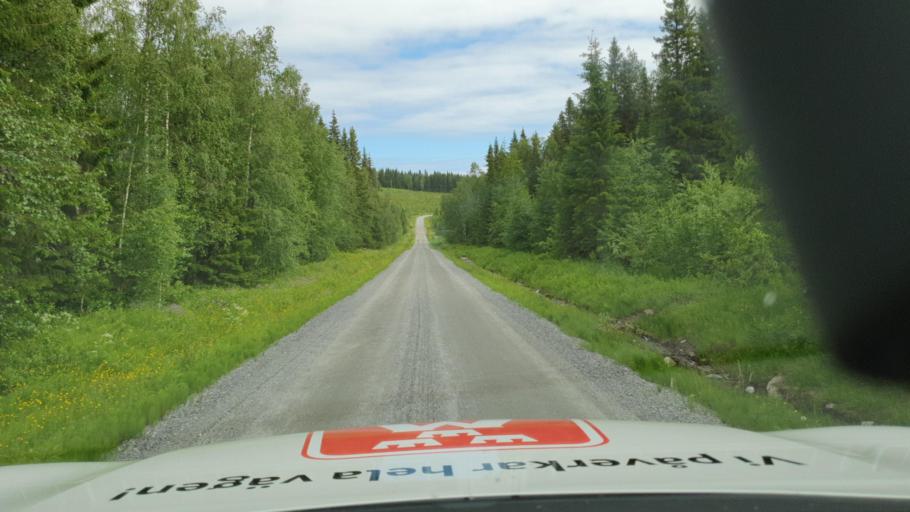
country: SE
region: Vaesterbotten
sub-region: Skelleftea Kommun
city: Langsele
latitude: 64.6437
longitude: 20.2773
